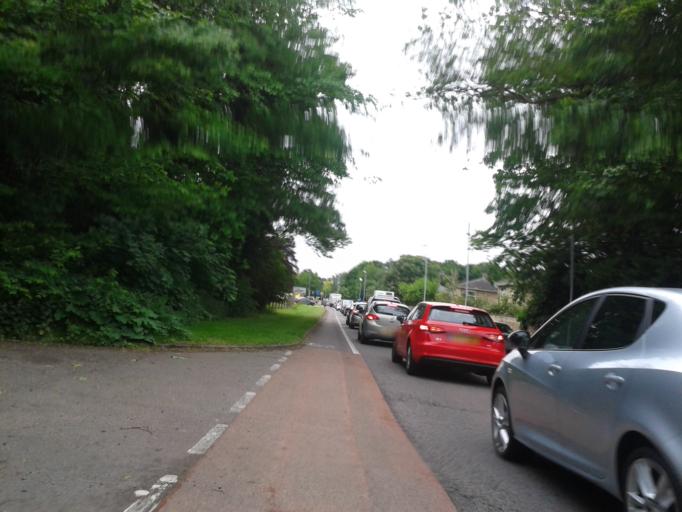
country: GB
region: England
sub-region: Cambridgeshire
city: Histon
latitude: 52.2395
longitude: 0.1128
